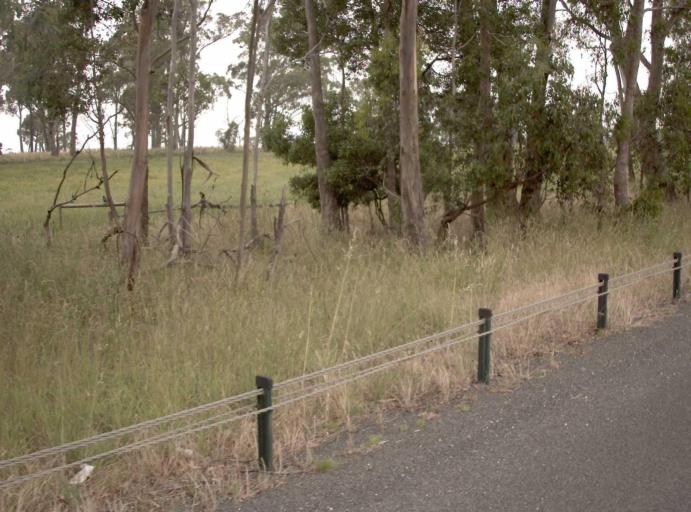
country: AU
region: Victoria
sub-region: Latrobe
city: Morwell
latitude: -38.2837
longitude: 146.3203
